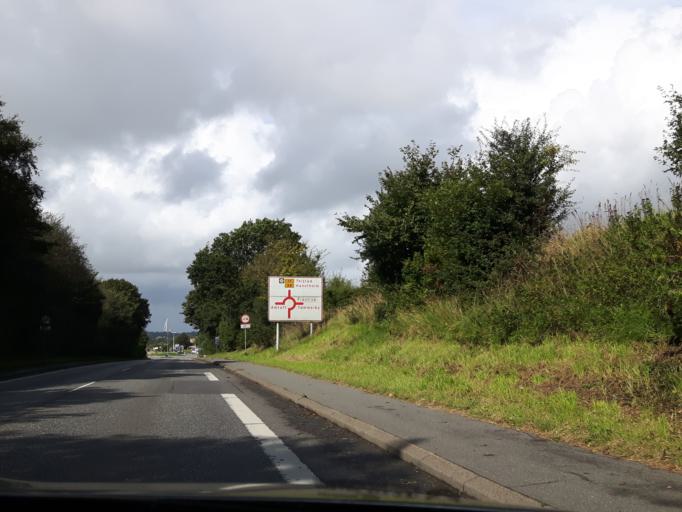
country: DK
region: North Denmark
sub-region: Morso Kommune
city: Nykobing Mors
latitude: 57.0344
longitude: 8.9740
